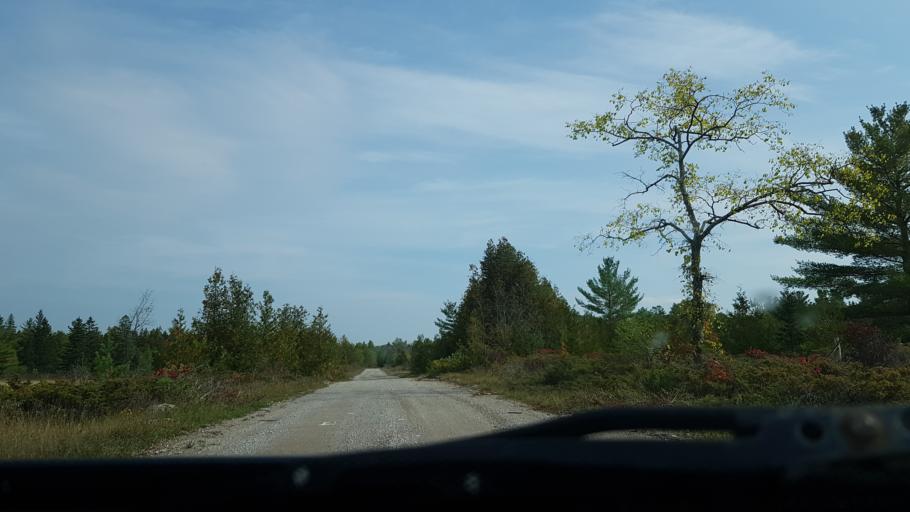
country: CA
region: Ontario
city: Orillia
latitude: 44.6839
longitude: -79.0559
